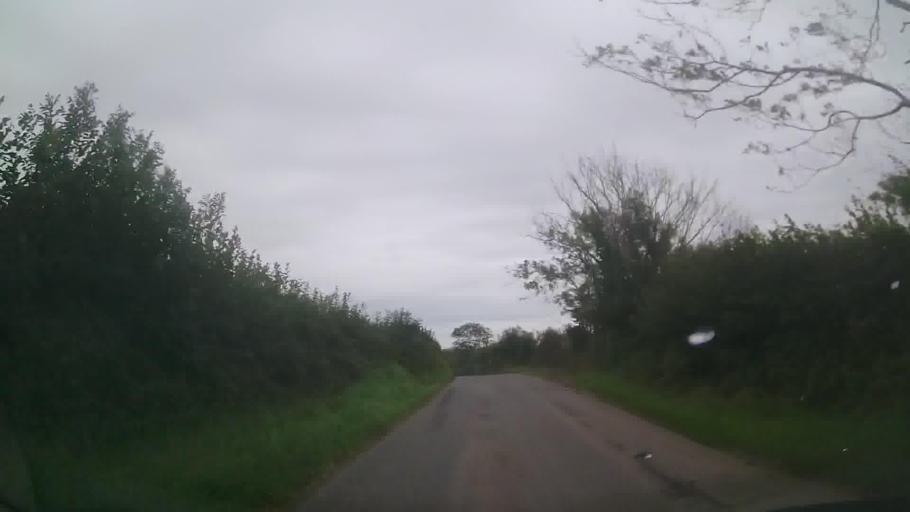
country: GB
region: Wales
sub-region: Carmarthenshire
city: Whitland
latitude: 51.7461
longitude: -4.6195
